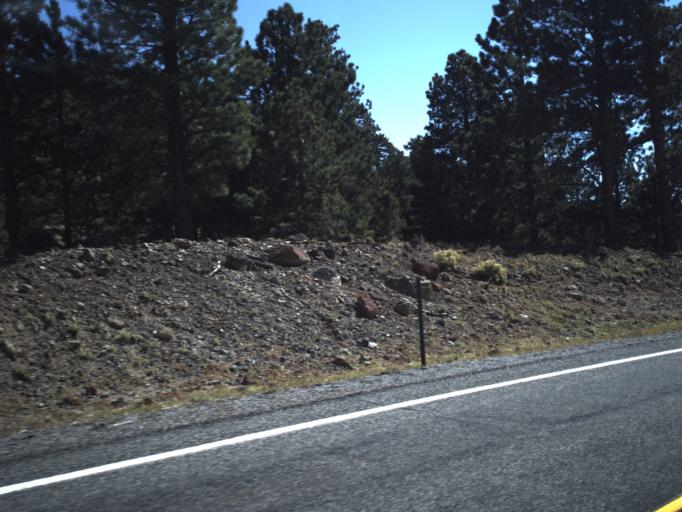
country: US
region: Utah
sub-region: Wayne County
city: Loa
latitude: 38.1194
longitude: -111.3258
